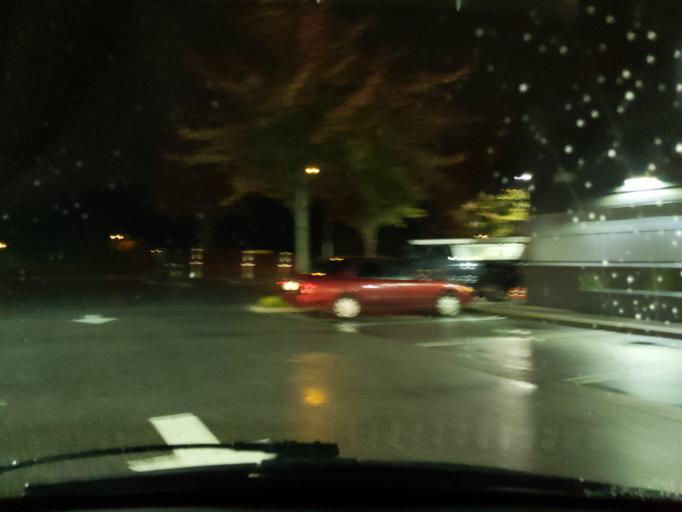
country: CA
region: British Columbia
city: Surrey
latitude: 49.1912
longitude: -122.8208
